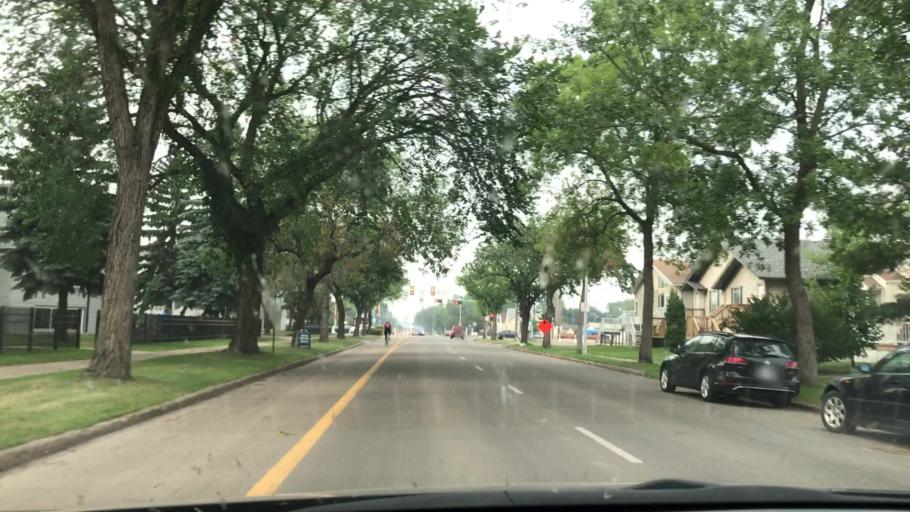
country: CA
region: Alberta
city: Edmonton
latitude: 53.5691
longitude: -113.5412
